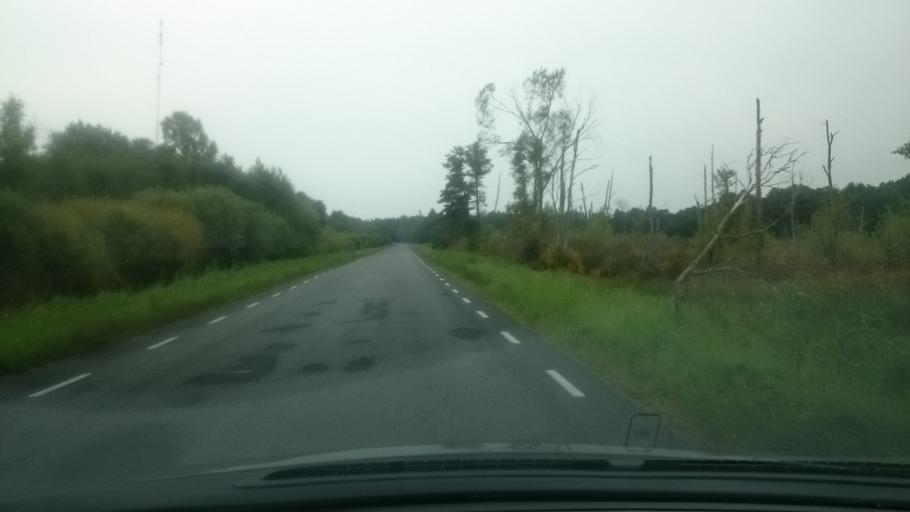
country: EE
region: Harju
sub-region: Raasiku vald
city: Raasiku
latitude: 59.5048
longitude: 25.2622
